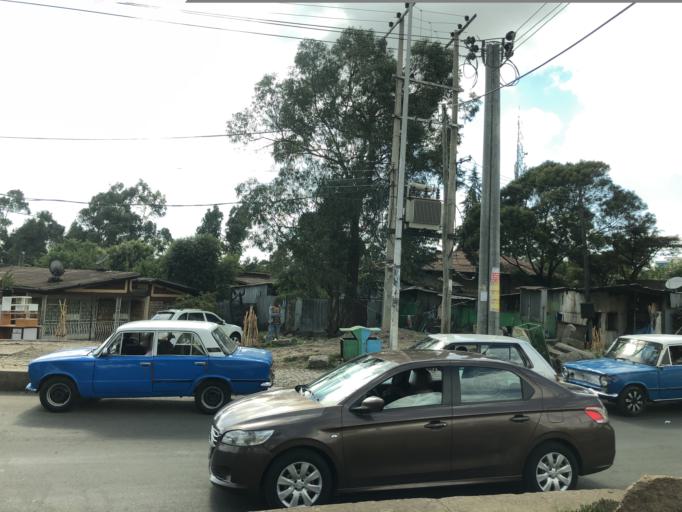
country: ET
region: Adis Abeba
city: Addis Ababa
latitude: 9.0229
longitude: 38.7810
